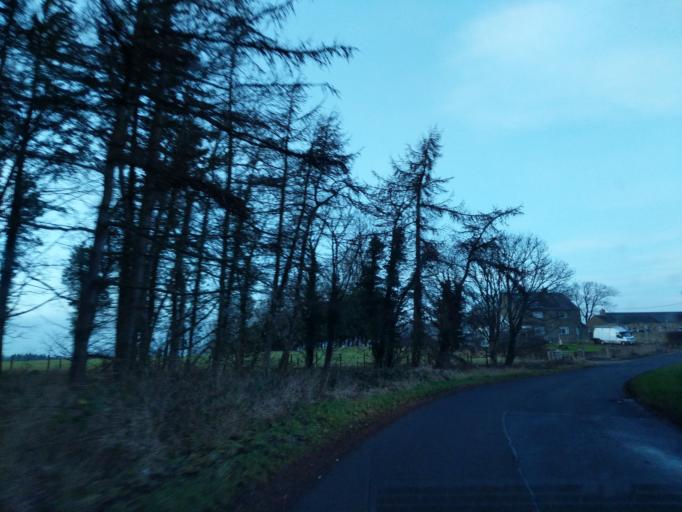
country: GB
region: Scotland
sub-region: Midlothian
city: Bonnyrigg
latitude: 55.8551
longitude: -3.0988
